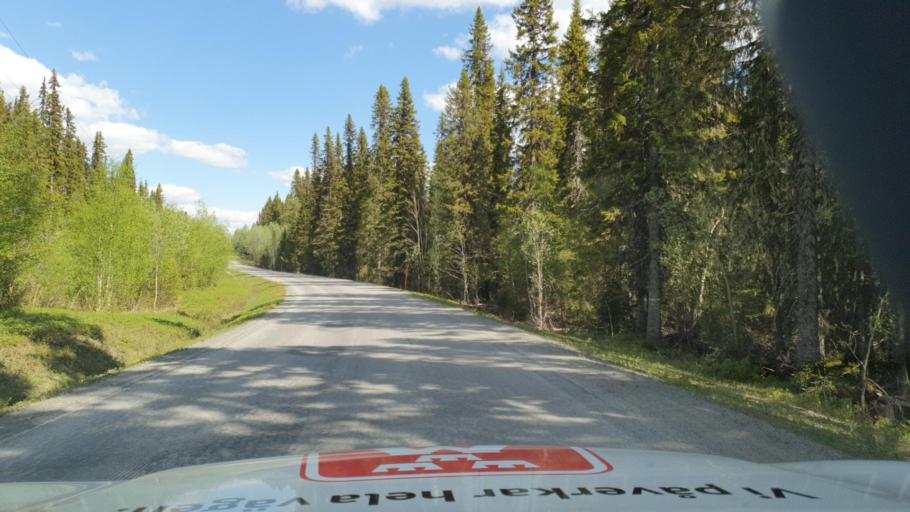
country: SE
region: Jaemtland
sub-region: Krokoms Kommun
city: Krokom
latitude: 63.6796
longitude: 14.2683
